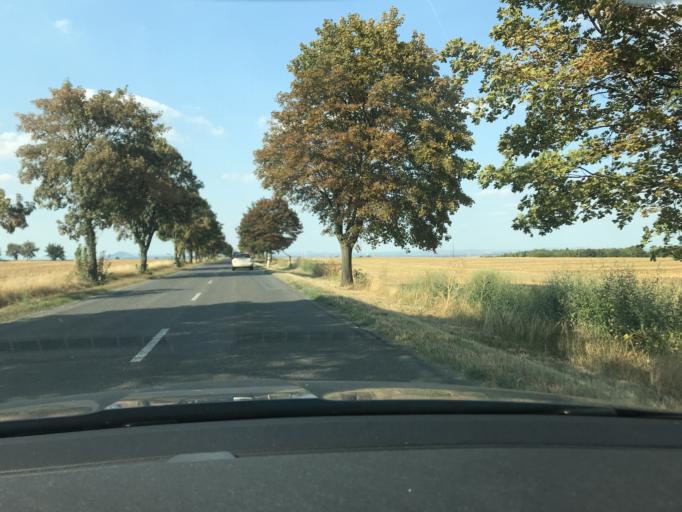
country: CZ
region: Central Bohemia
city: Kralupy nad Vltavou
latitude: 50.2083
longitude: 14.3158
